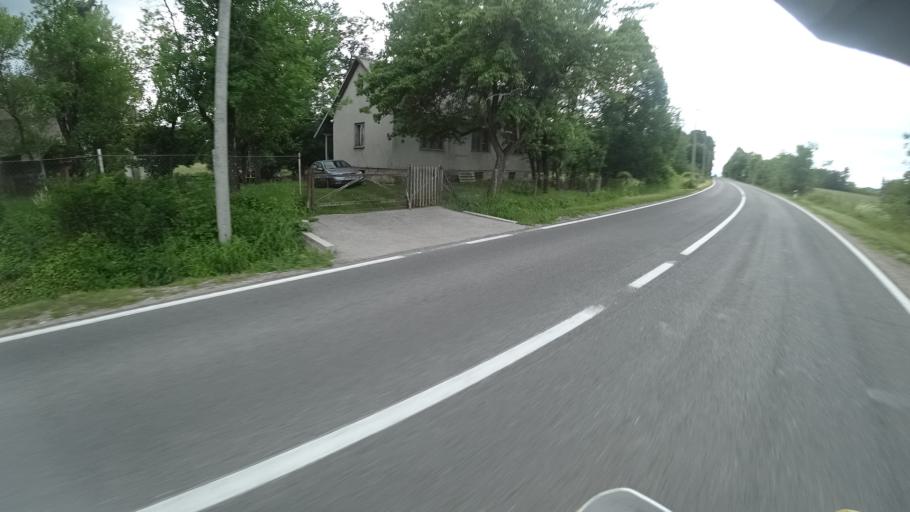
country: HR
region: Licko-Senjska
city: Gospic
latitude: 44.4971
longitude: 15.4580
